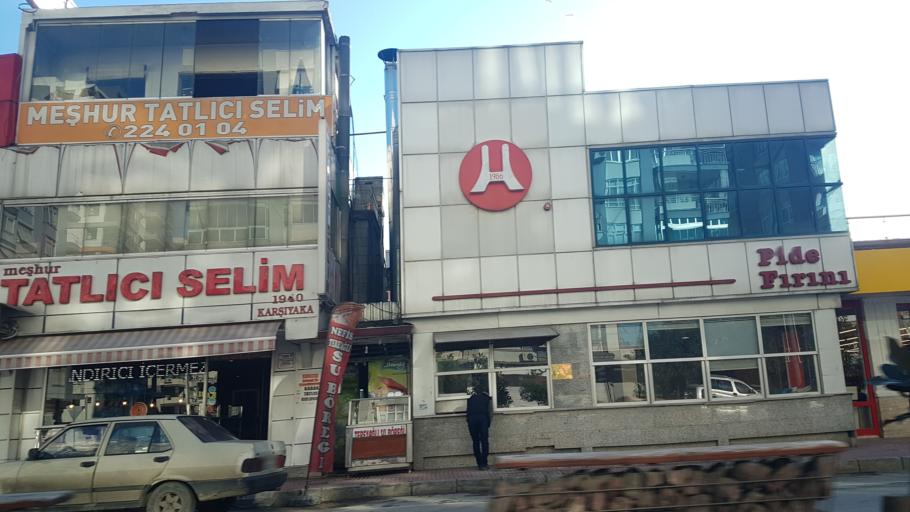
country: TR
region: Adana
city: Adana
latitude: 37.0209
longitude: 35.3159
